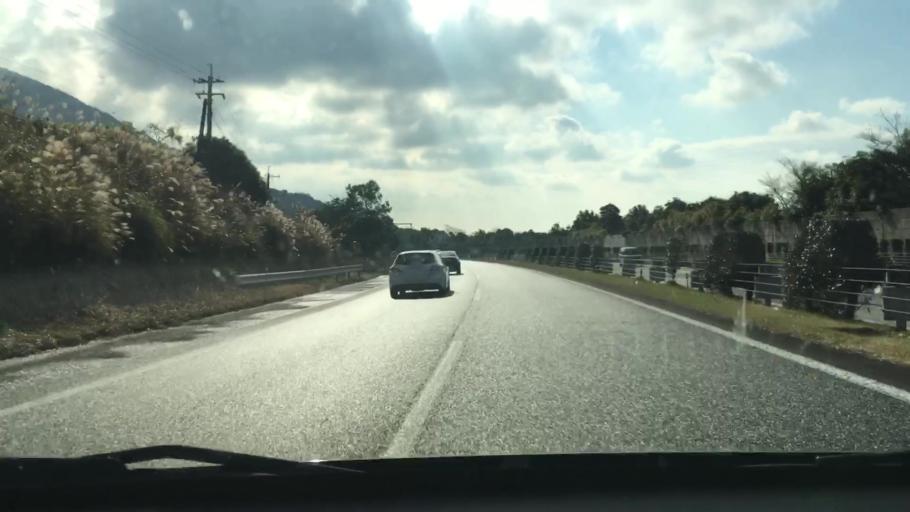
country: JP
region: Kumamoto
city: Yatsushiro
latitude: 32.5384
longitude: 130.6744
